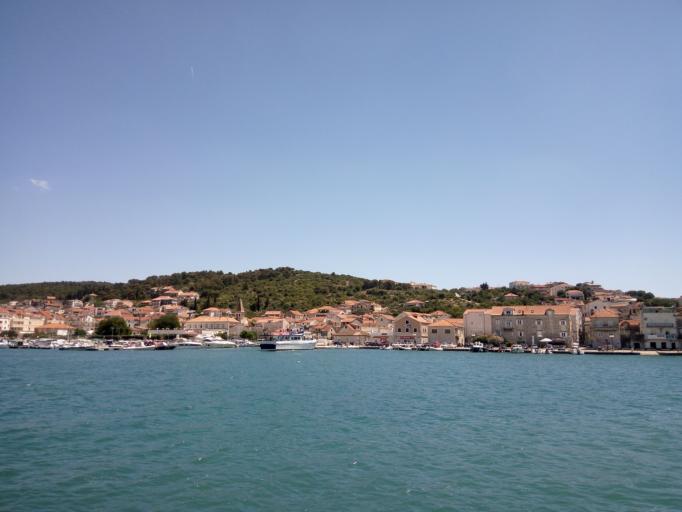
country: HR
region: Splitsko-Dalmatinska
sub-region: Grad Trogir
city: Trogir
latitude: 43.5166
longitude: 16.2525
